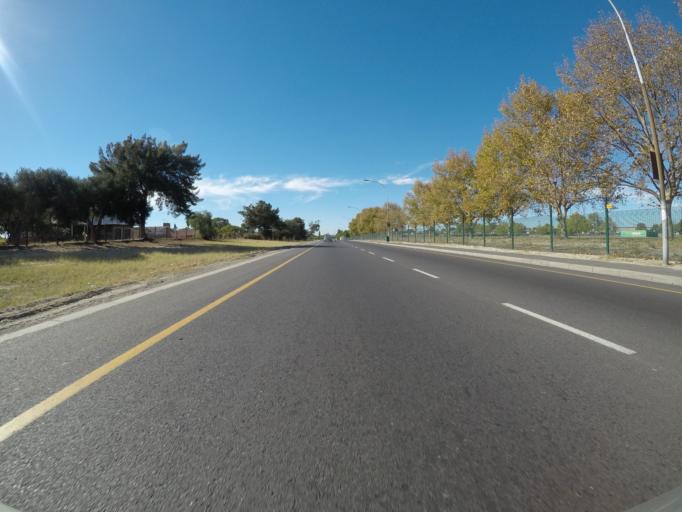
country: ZA
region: Western Cape
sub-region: City of Cape Town
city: Kraaifontein
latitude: -33.9394
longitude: 18.6768
